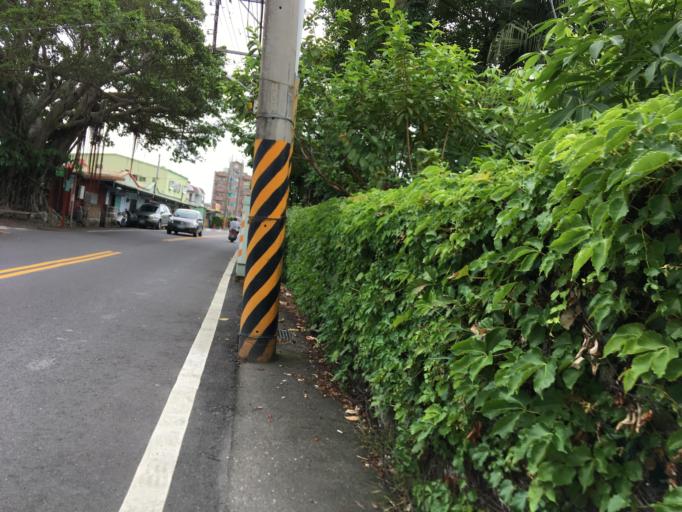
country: TW
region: Taiwan
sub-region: Yilan
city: Yilan
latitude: 24.6967
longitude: 121.8114
